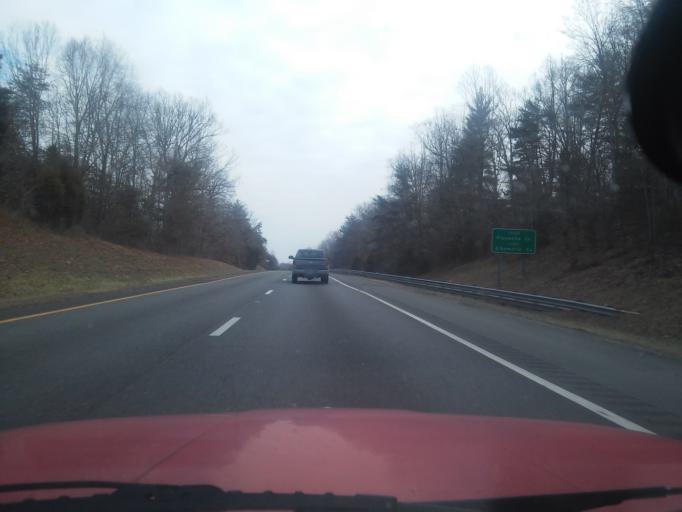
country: US
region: Virginia
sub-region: Fluvanna County
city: Lake Monticello
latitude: 37.9962
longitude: -78.3153
